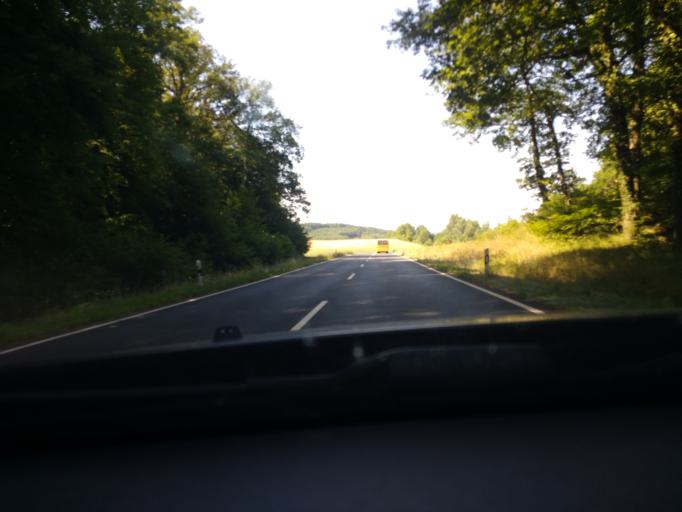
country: DE
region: Rheinland-Pfalz
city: Neuerburg
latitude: 50.0052
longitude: 6.9736
